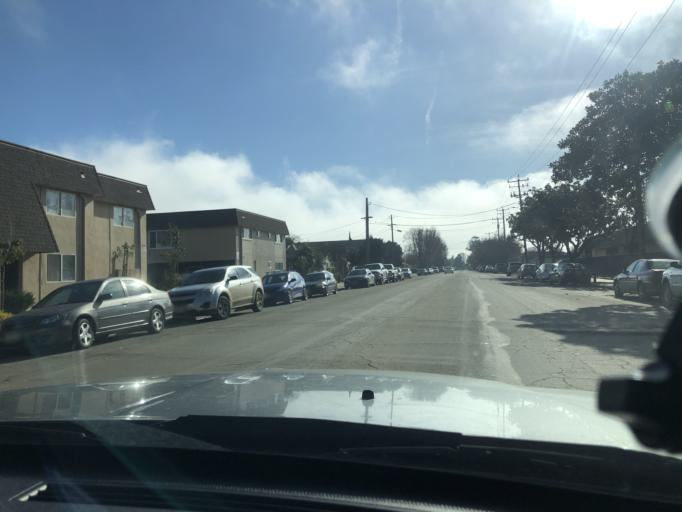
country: US
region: California
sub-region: Monterey County
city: King City
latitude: 36.2103
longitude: -121.1262
